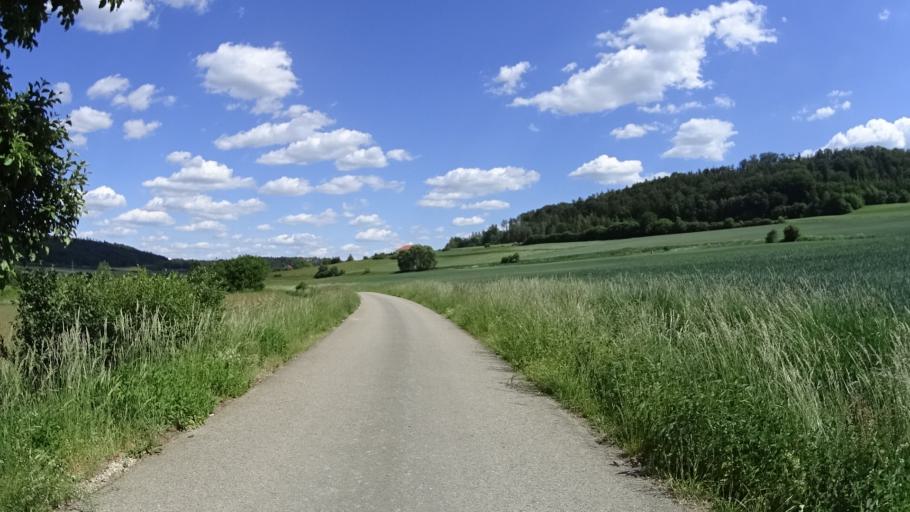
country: DE
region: Bavaria
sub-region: Regierungsbezirk Mittelfranken
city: Greding
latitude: 49.0638
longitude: 11.3098
